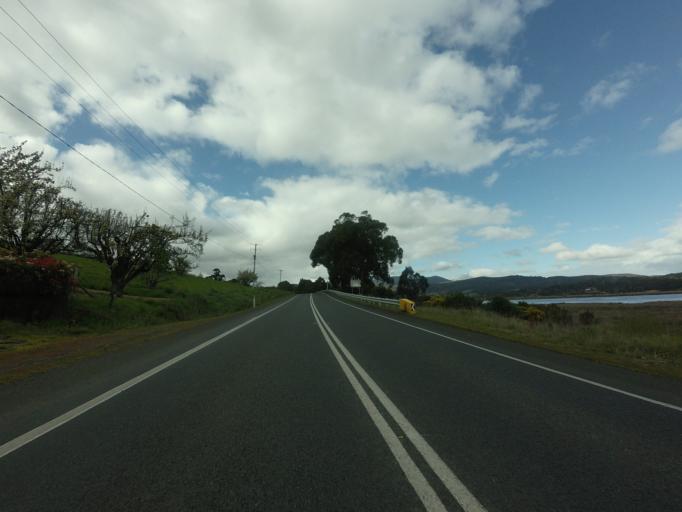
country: AU
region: Tasmania
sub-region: Huon Valley
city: Franklin
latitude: -43.1123
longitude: 146.9956
